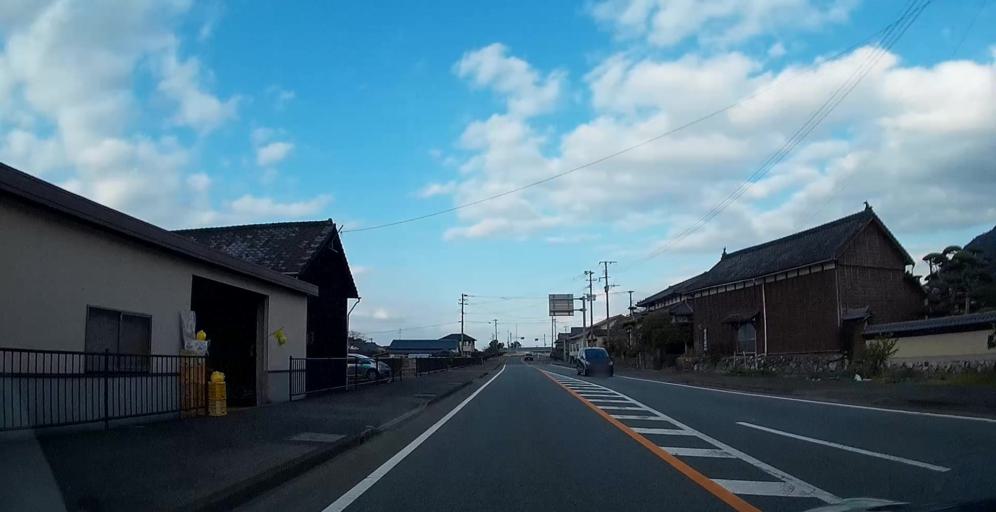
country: JP
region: Kumamoto
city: Yatsushiro
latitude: 32.5279
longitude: 130.6608
